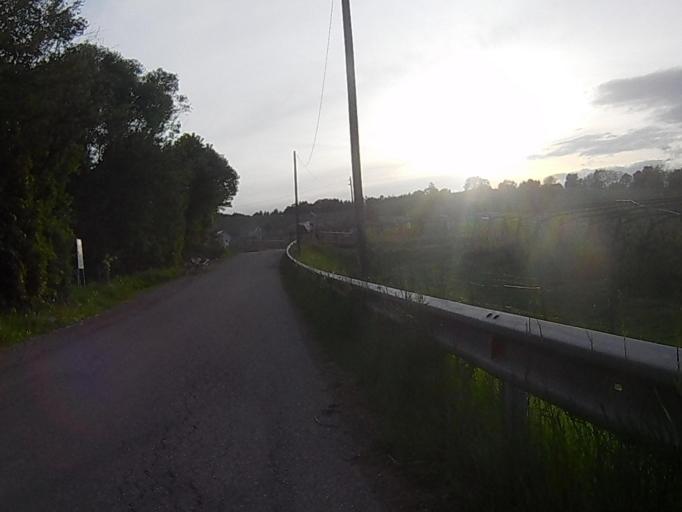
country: SI
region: Maribor
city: Pekre
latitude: 46.5419
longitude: 15.5887
